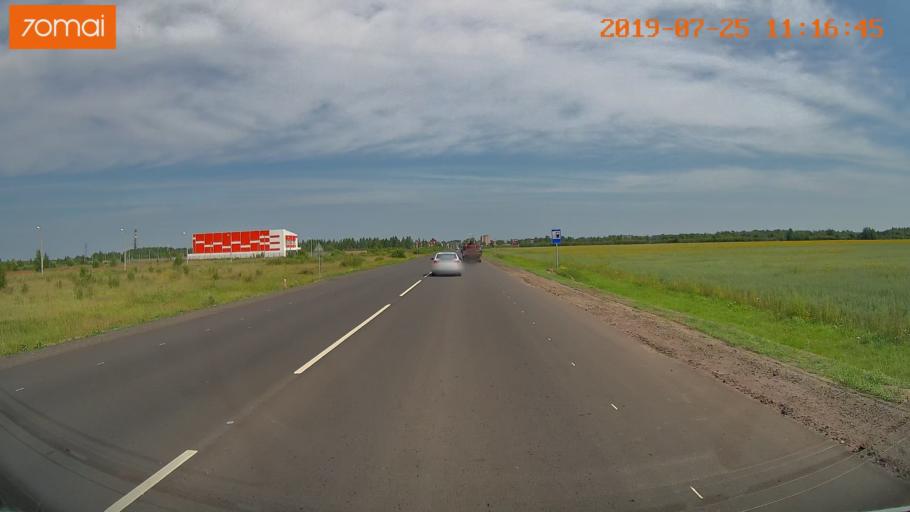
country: RU
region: Ivanovo
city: Privolzhsk
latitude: 57.3615
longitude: 41.2664
